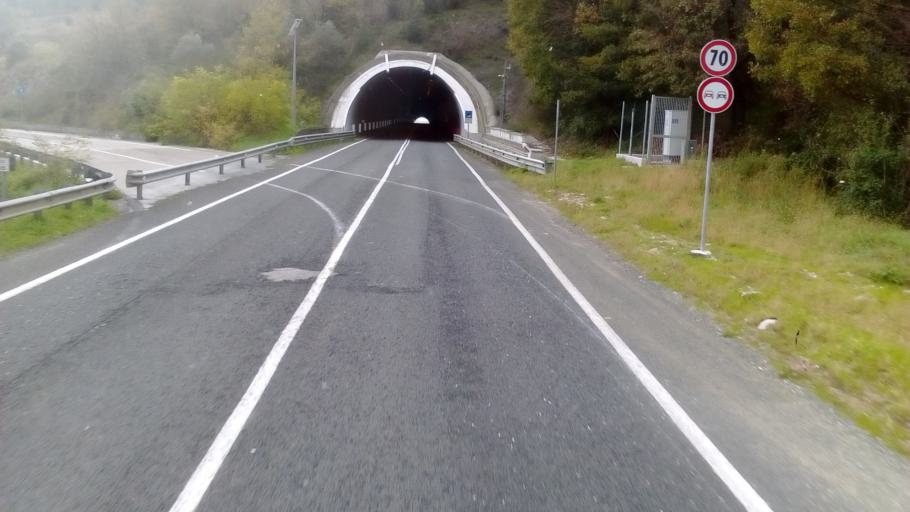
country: IT
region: Molise
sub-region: Provincia di Isernia
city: Macchia d'Isernia
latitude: 41.5563
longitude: 14.1687
